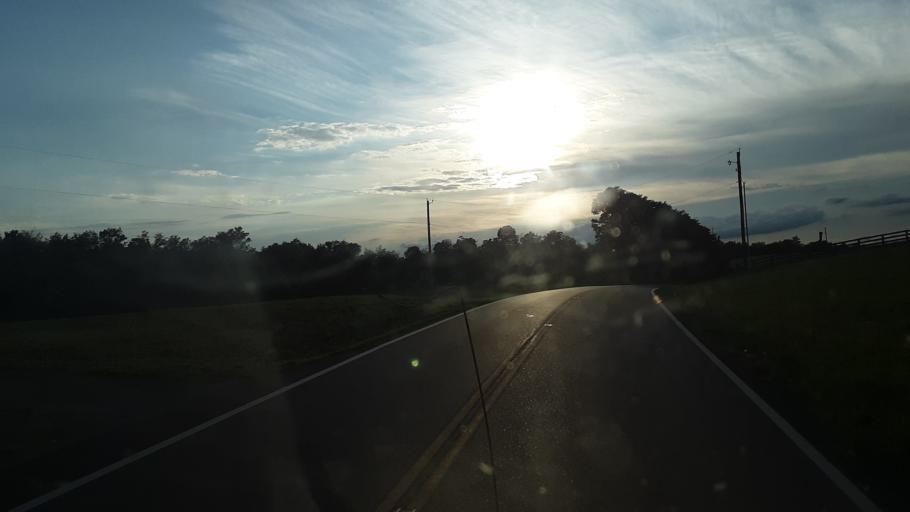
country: US
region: Ohio
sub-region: Harrison County
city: Cadiz
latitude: 40.3993
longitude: -81.0176
